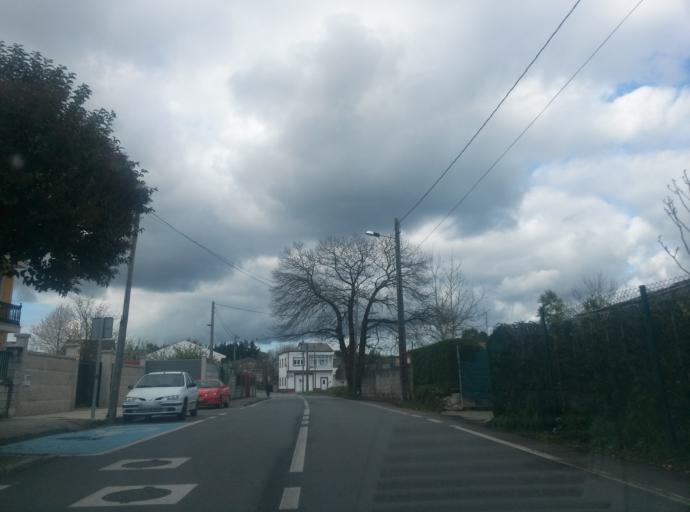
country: ES
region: Galicia
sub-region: Provincia de Lugo
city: Lugo
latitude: 43.0260
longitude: -7.5537
